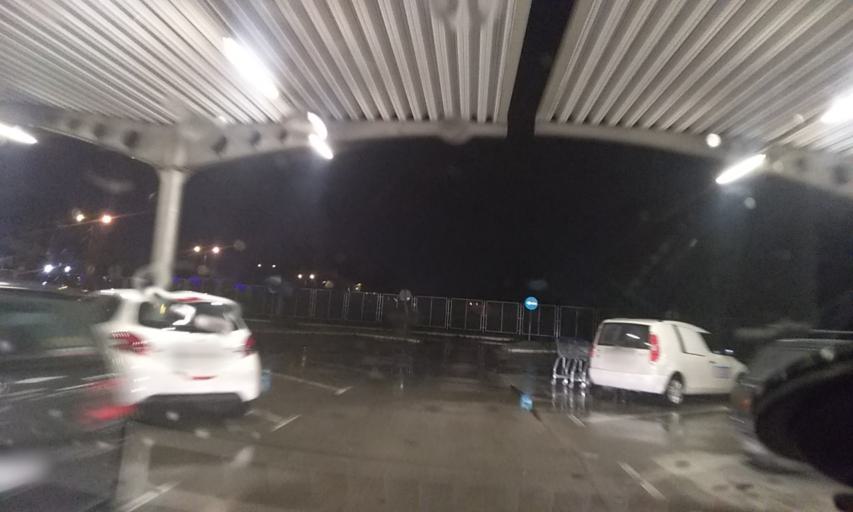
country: RS
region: Central Serbia
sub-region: Nisavski Okrug
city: Nis
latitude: 43.3180
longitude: 21.8422
